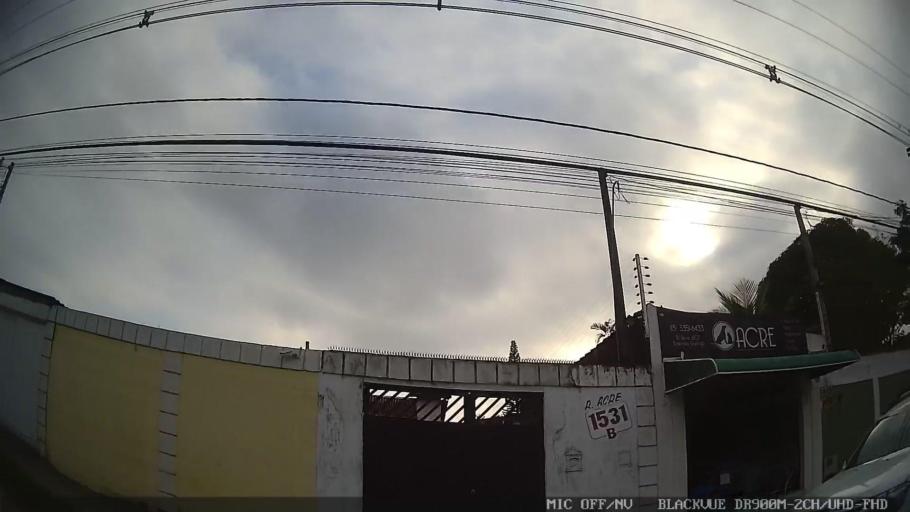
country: BR
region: Sao Paulo
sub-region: Guaruja
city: Guaruja
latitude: -23.9708
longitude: -46.2109
